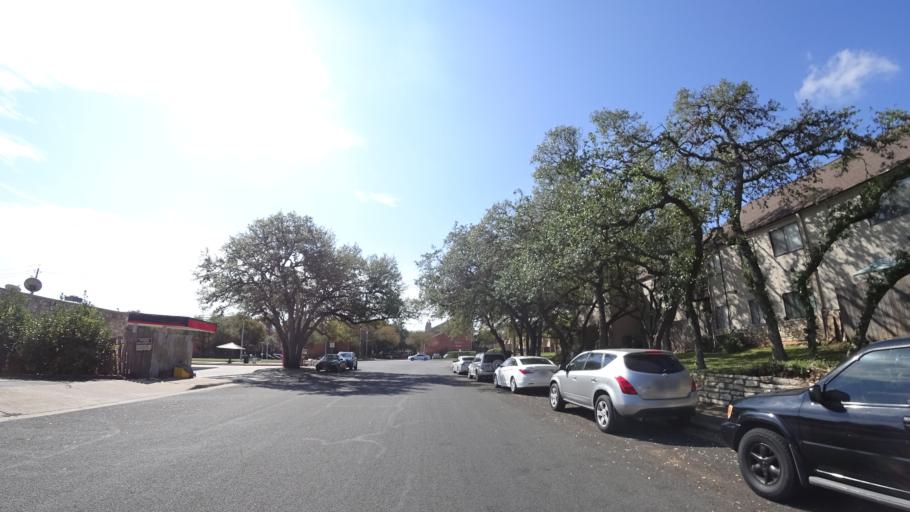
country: US
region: Texas
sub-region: Travis County
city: Shady Hollow
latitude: 30.2087
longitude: -97.8176
